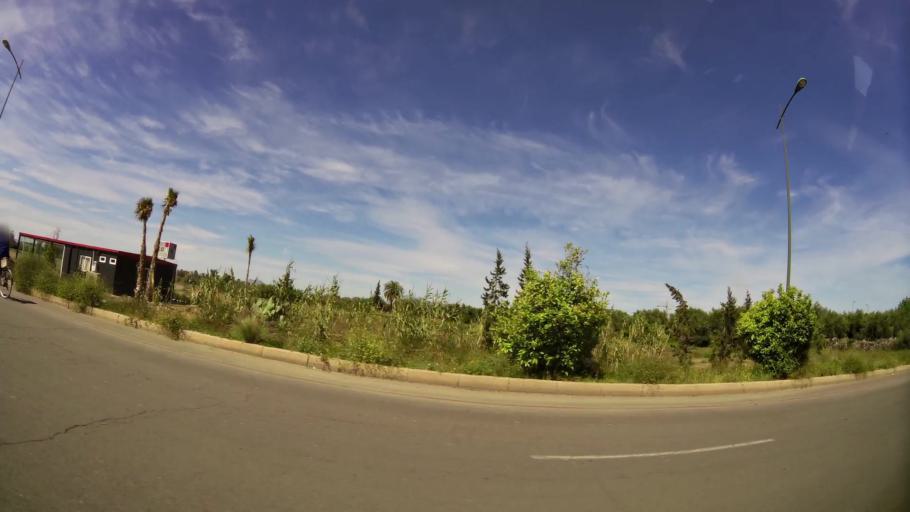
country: MA
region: Marrakech-Tensift-Al Haouz
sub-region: Marrakech
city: Marrakesh
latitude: 31.6539
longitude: -8.0678
